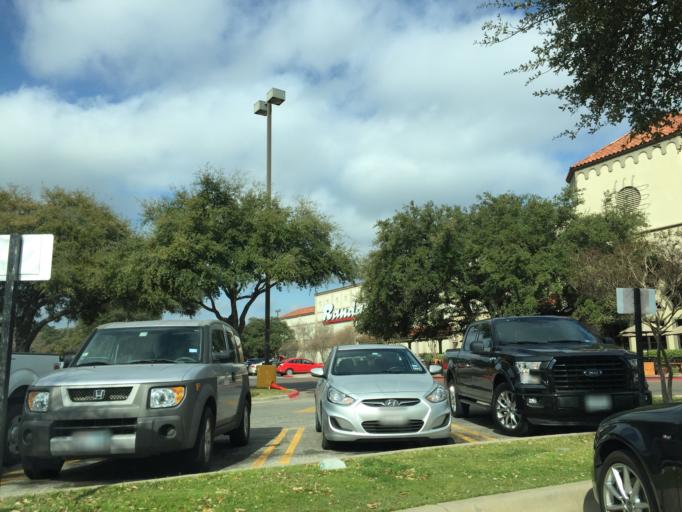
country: US
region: Texas
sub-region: Williamson County
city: Jollyville
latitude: 30.4016
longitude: -97.7469
